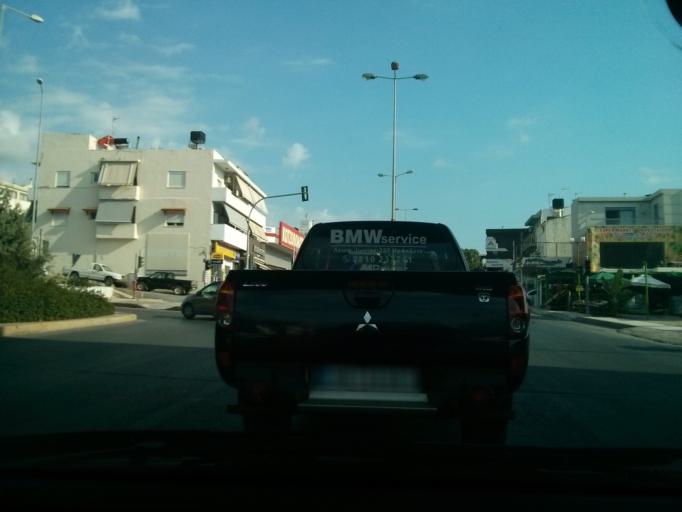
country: GR
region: Crete
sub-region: Nomos Irakleiou
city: Irakleion
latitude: 35.3206
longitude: 25.1436
